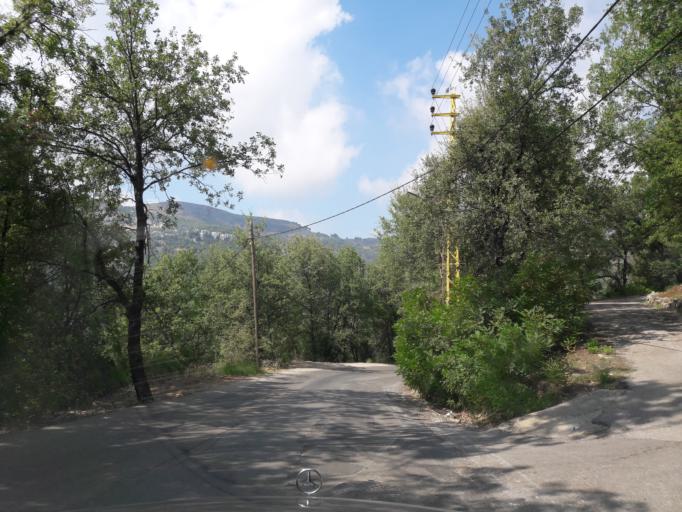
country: LB
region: Mont-Liban
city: Djounie
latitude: 33.9587
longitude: 35.7771
